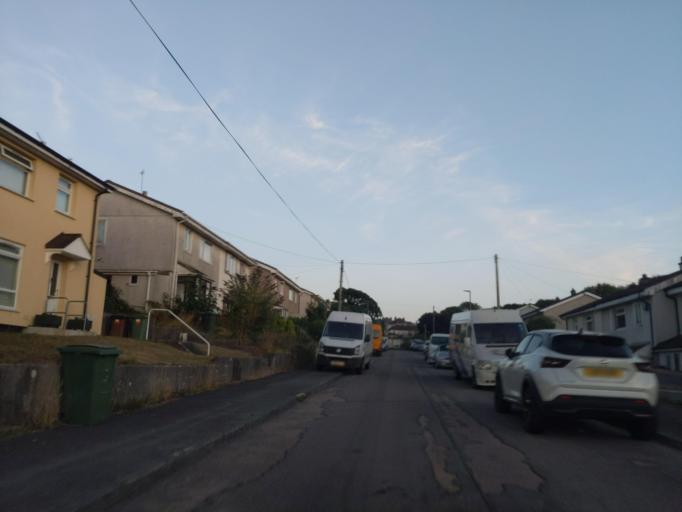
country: GB
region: England
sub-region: Plymouth
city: Plymouth
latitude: 50.3976
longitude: -4.1636
